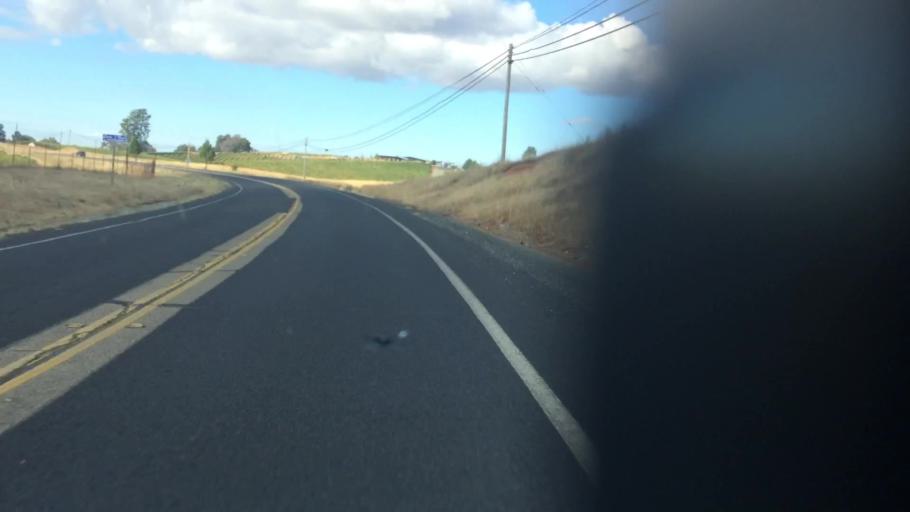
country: US
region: California
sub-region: Amador County
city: Plymouth
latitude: 38.5310
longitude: -120.8041
